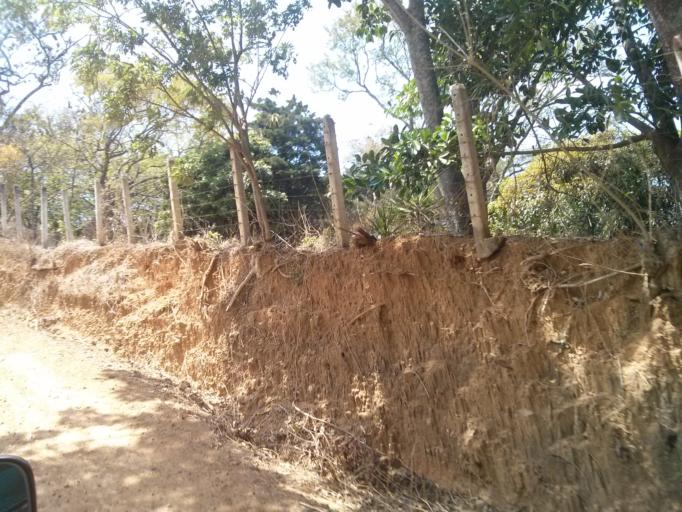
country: CR
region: Heredia
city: Colon
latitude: 9.9148
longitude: -84.2178
